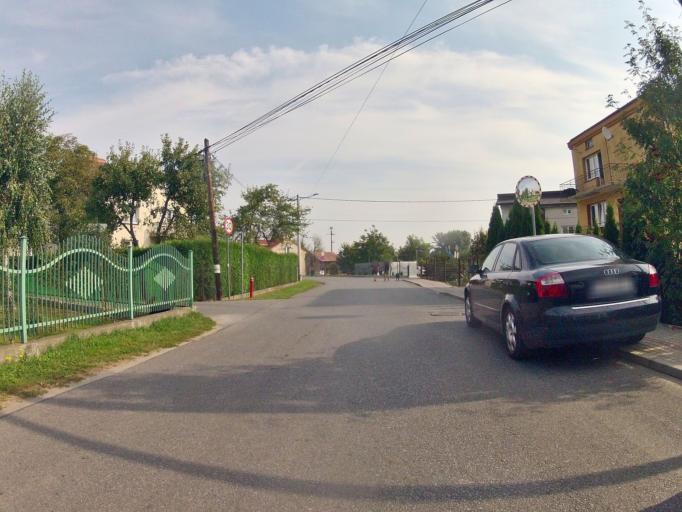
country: PL
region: Subcarpathian Voivodeship
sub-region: Powiat jasielski
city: Jaslo
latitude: 49.7345
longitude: 21.4526
